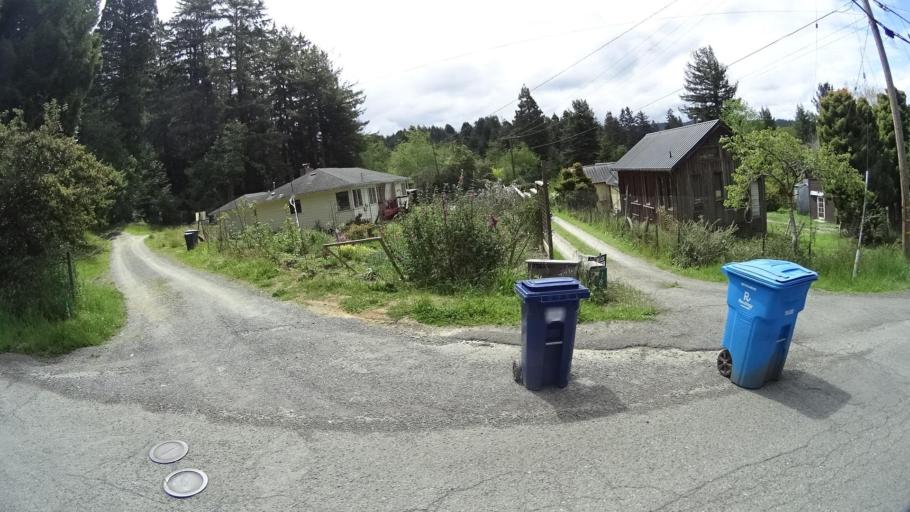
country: US
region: California
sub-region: Humboldt County
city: Bayside
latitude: 40.8470
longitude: -124.0625
